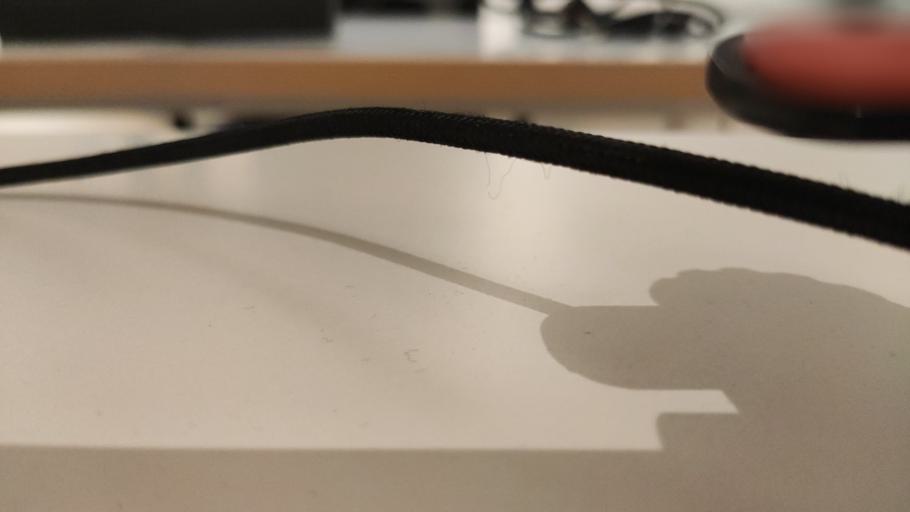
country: RU
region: Moskovskaya
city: Dorokhovo
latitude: 55.5116
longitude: 36.3471
